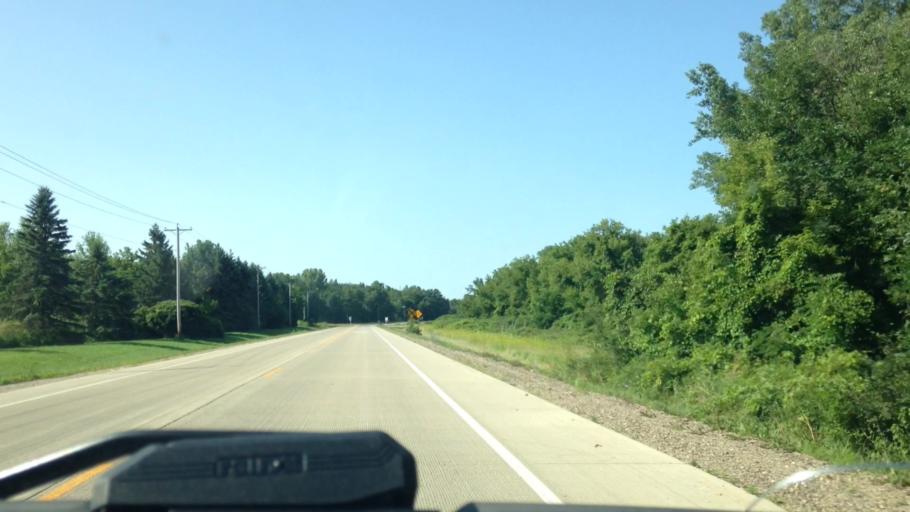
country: US
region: Wisconsin
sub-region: Dodge County
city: Mayville
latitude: 43.4781
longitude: -88.5548
